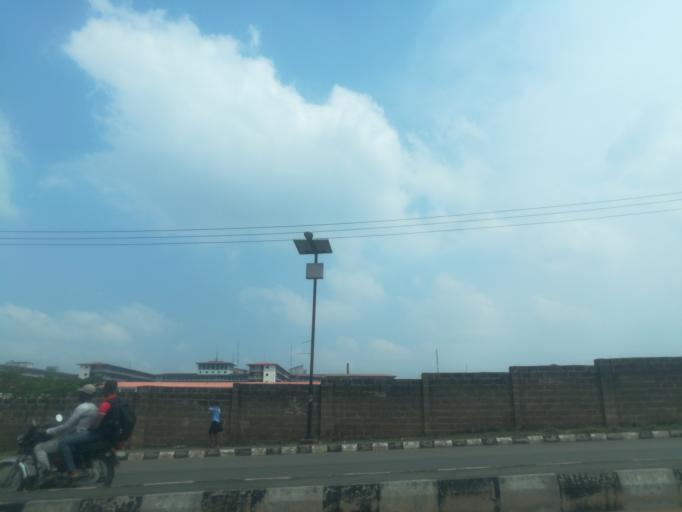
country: NG
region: Oyo
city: Ibadan
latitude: 7.3985
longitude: 3.9017
